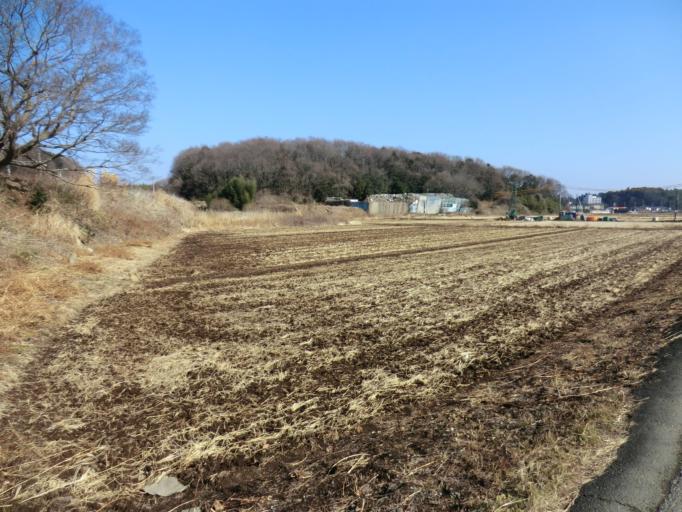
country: JP
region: Ibaraki
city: Naka
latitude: 36.0552
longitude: 140.1850
